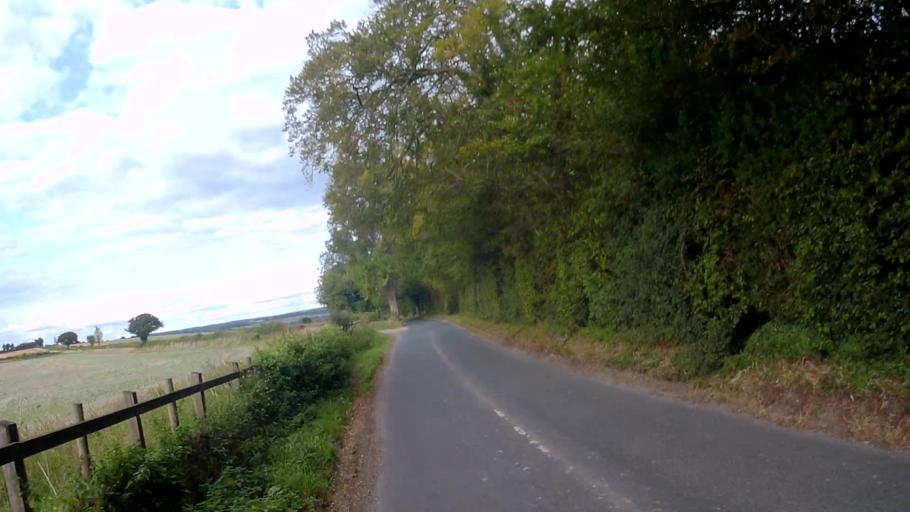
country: GB
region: England
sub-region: Hampshire
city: Kings Worthy
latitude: 51.1355
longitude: -1.1979
